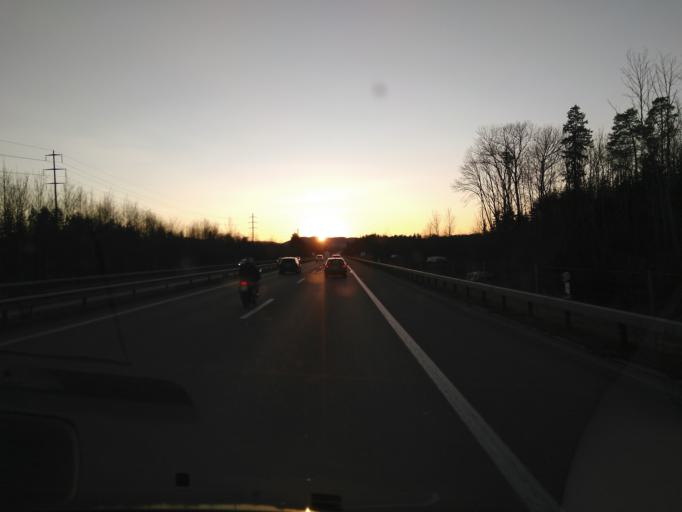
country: CH
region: Saint Gallen
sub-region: Wahlkreis Wil
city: Zuzwil
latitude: 47.4595
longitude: 9.0891
